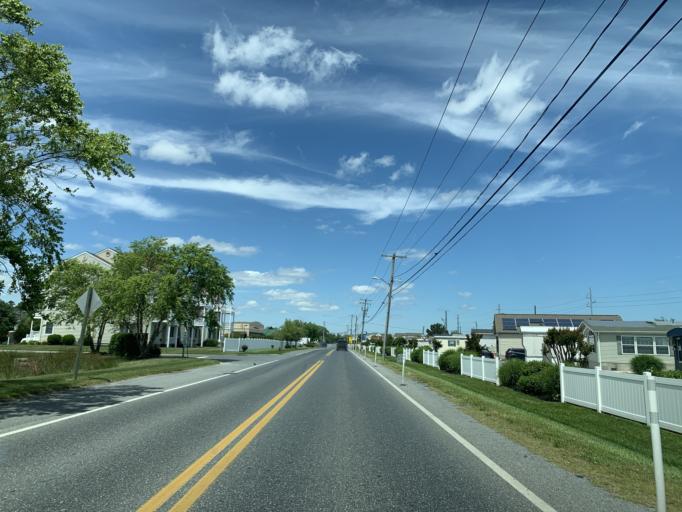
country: US
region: Maryland
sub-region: Worcester County
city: West Ocean City
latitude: 38.3333
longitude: -75.1060
